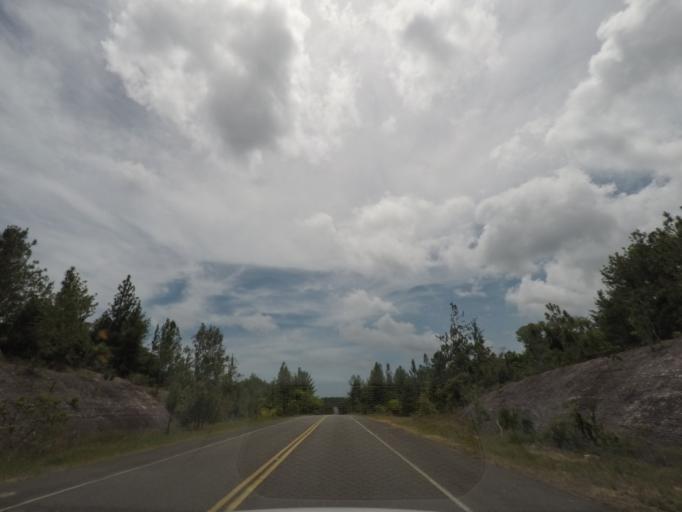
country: BR
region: Bahia
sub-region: Entre Rios
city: Entre Rios
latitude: -12.1211
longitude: -37.7887
